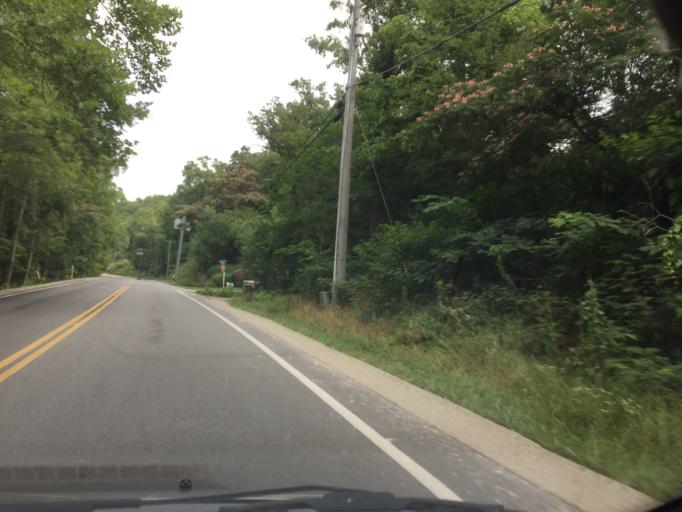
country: US
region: Tennessee
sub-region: Hamilton County
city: Apison
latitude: 34.9929
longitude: -85.0765
